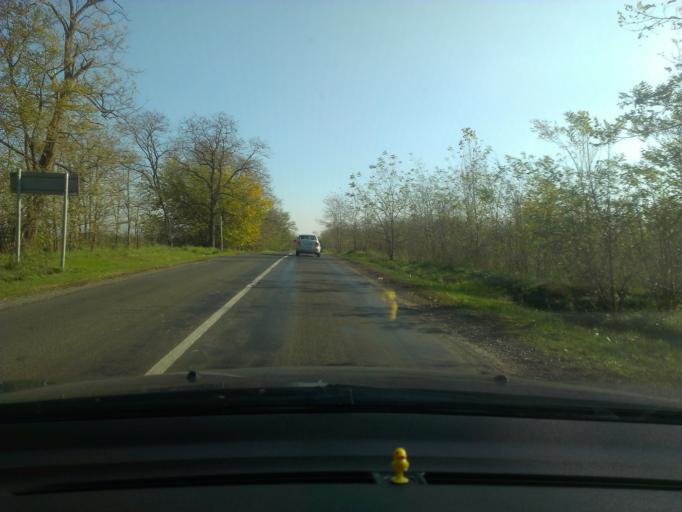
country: HU
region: Komarom-Esztergom
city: Naszaly
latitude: 47.6858
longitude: 18.2323
